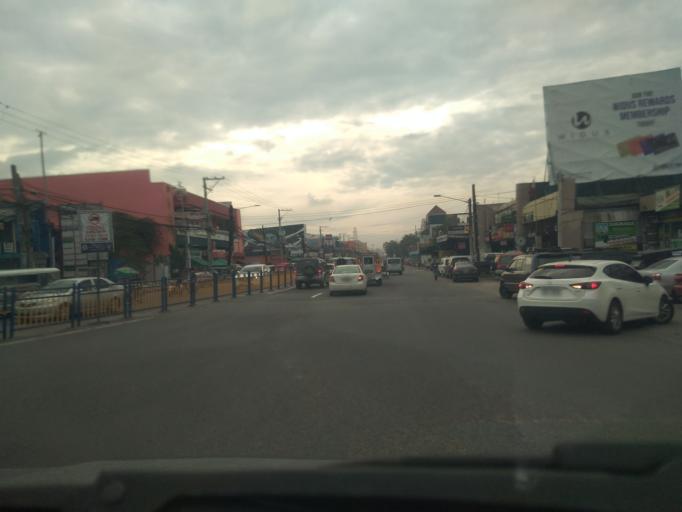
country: PH
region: Central Luzon
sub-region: Province of Pampanga
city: San Fernando
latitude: 15.0388
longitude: 120.6809
